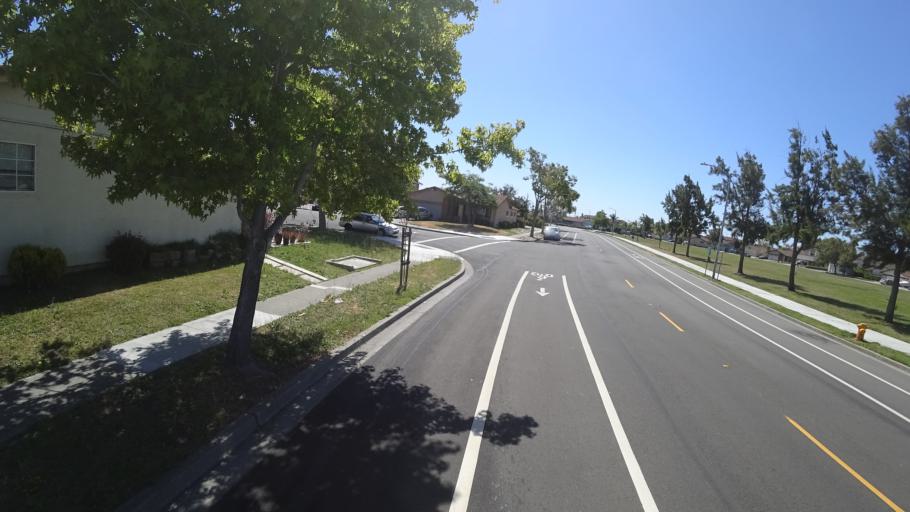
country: US
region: California
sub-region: Alameda County
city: Hayward
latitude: 37.6207
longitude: -122.0941
